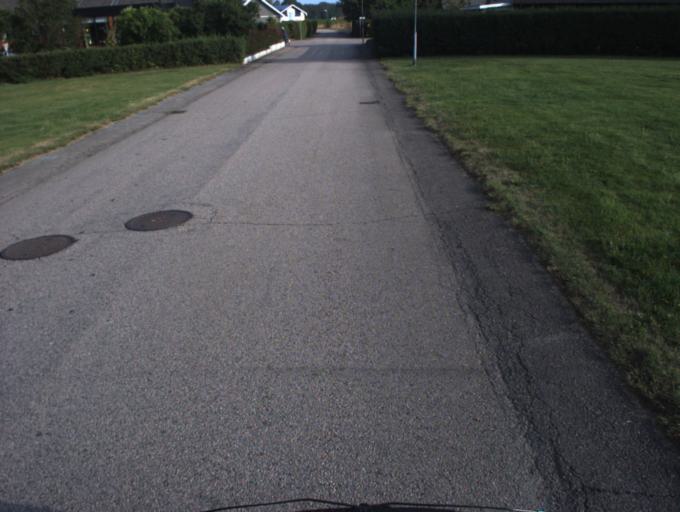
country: SE
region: Skane
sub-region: Angelholms Kommun
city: Strovelstorp
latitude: 56.1413
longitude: 12.7838
